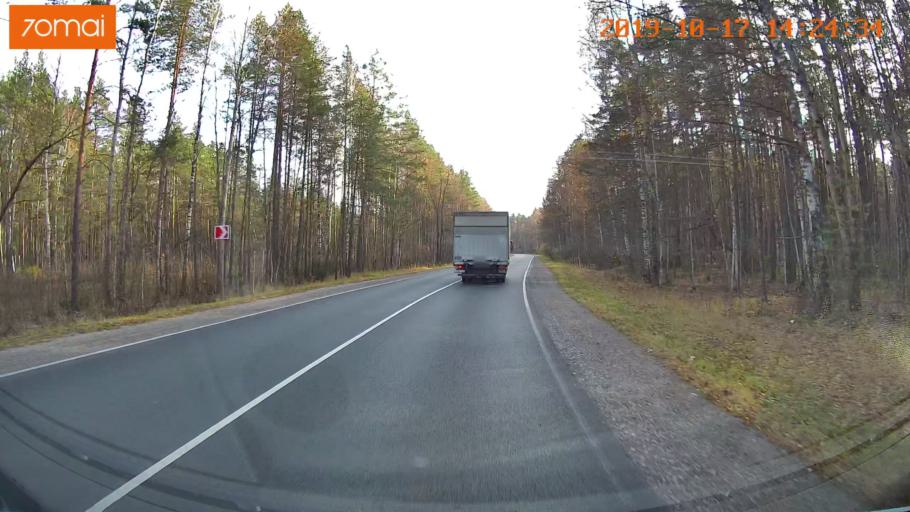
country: RU
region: Moskovskaya
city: Radovitskiy
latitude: 55.0082
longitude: 39.9696
